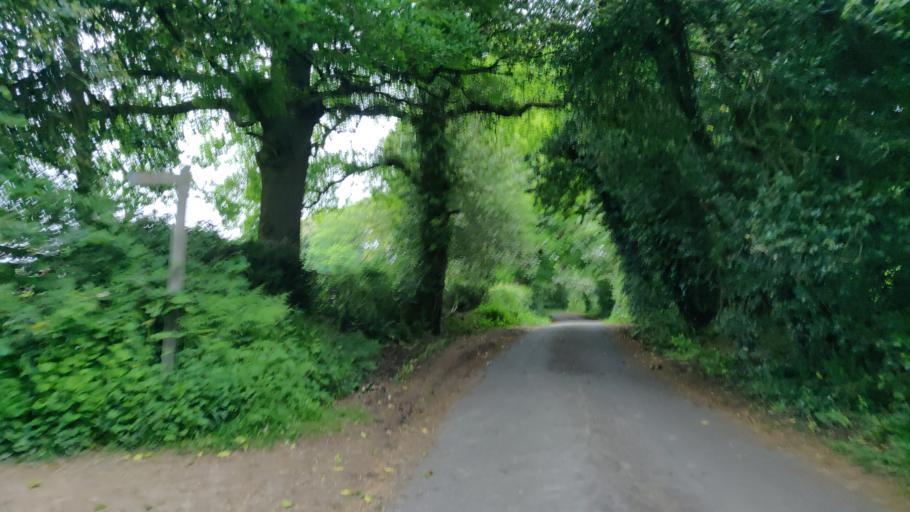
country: GB
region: England
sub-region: West Sussex
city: Southwater
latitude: 51.0219
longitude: -0.3302
